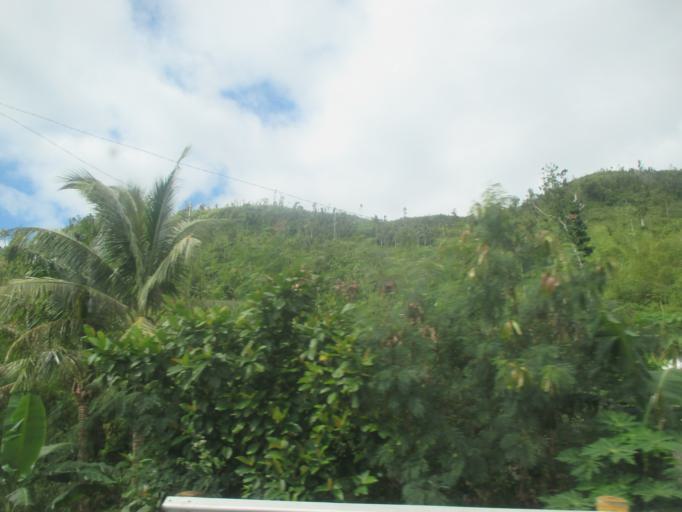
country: PH
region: Eastern Visayas
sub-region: Province of Eastern Samar
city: Lawa-an
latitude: 11.1142
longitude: 125.2449
